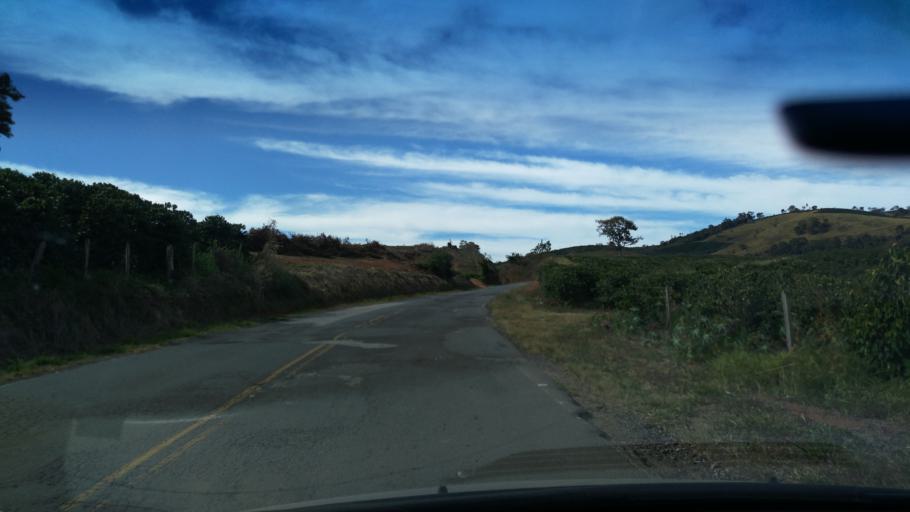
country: BR
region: Minas Gerais
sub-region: Andradas
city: Andradas
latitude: -22.0615
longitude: -46.3836
